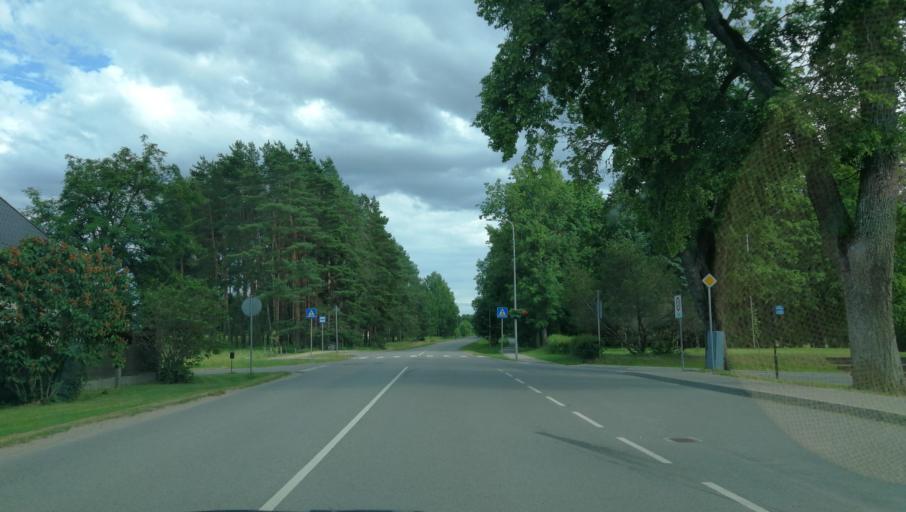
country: LV
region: Rujienas
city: Rujiena
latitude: 57.8947
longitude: 25.3386
